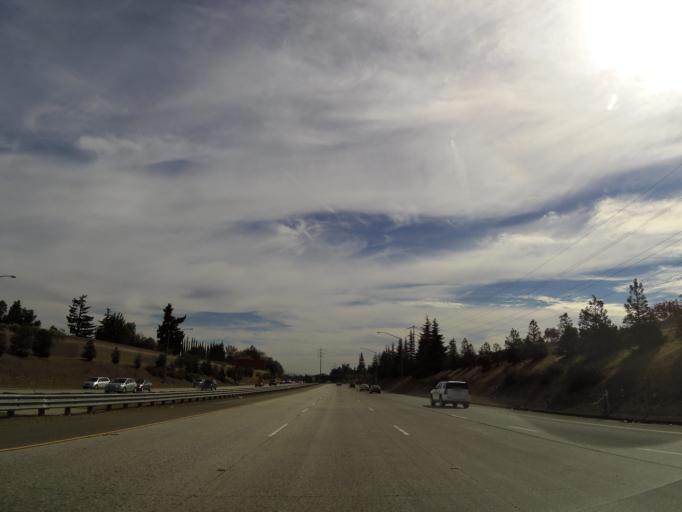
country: US
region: California
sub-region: Santa Clara County
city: Saratoga
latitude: 37.2750
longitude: -122.0044
